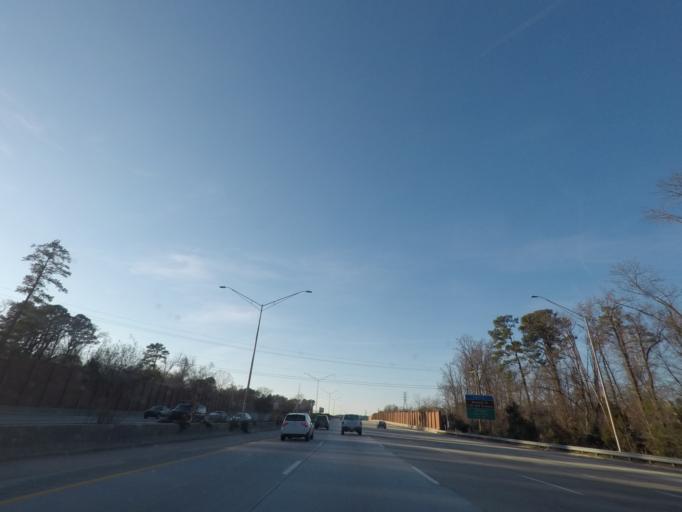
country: US
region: North Carolina
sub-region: Durham County
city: Durham
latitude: 36.0167
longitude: -78.8952
